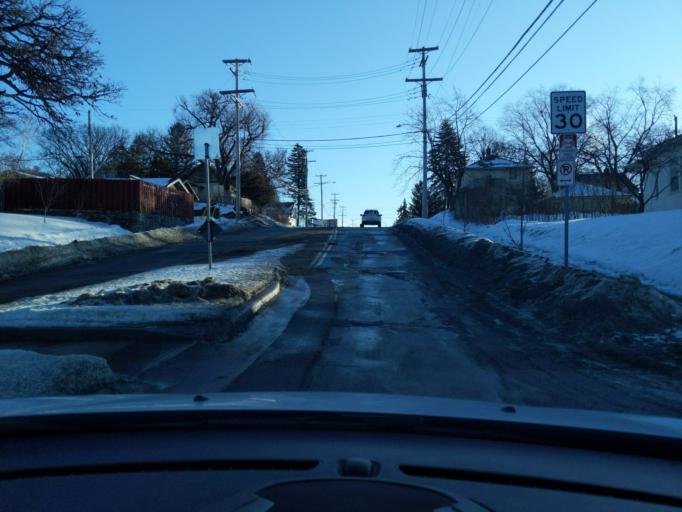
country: US
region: Minnesota
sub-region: Hennepin County
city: Richfield
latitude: 44.9270
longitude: -93.2499
